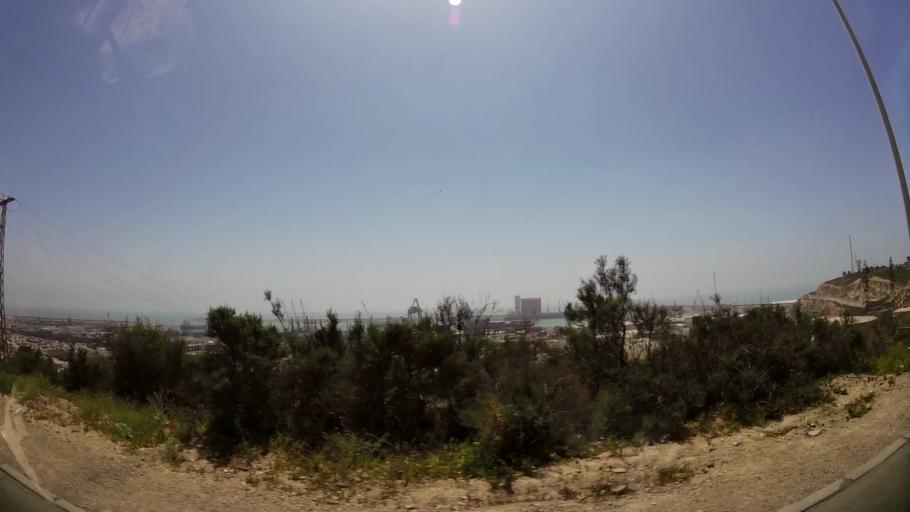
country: MA
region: Souss-Massa-Draa
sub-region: Agadir-Ida-ou-Tnan
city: Agadir
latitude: 30.4325
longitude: -9.6370
